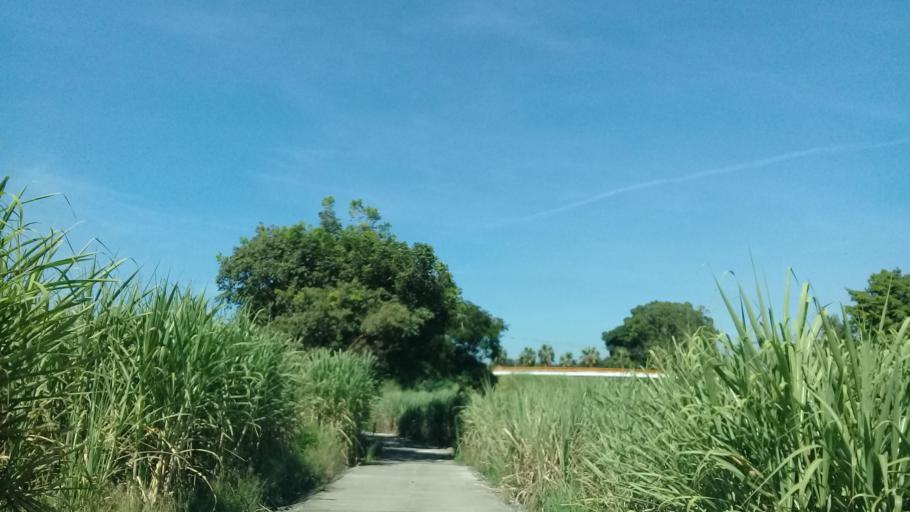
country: MX
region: Veracruz
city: Amatlan de los Reyes
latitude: 18.8591
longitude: -96.9027
